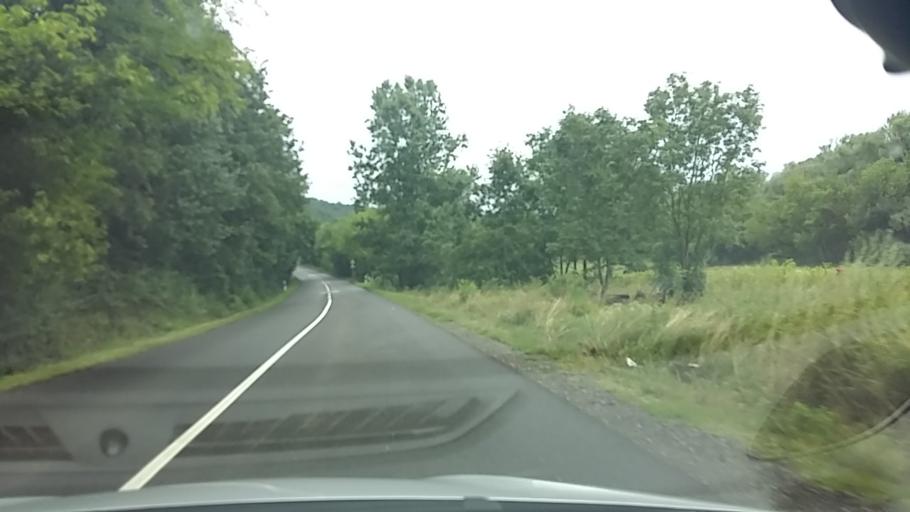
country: HU
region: Pest
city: Szob
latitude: 47.8548
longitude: 18.8167
